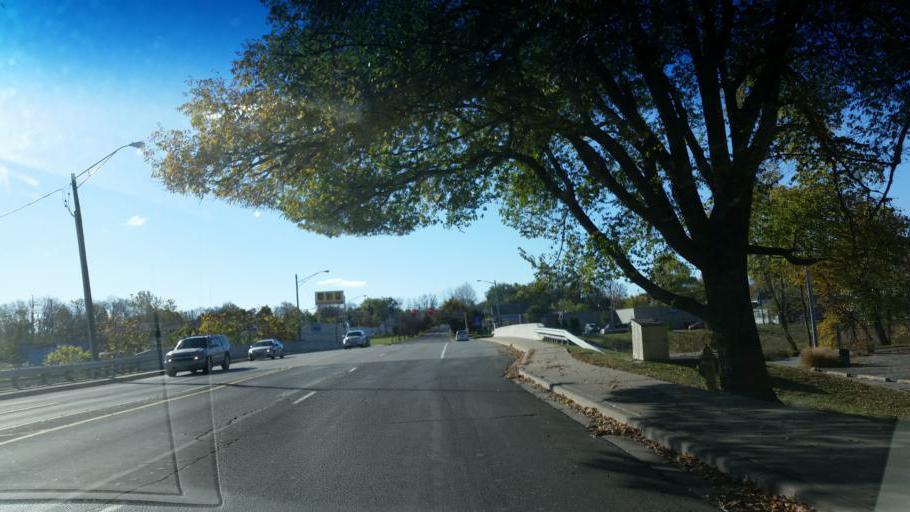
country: US
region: Indiana
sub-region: Howard County
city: Kokomo
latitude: 40.4848
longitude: -86.1338
